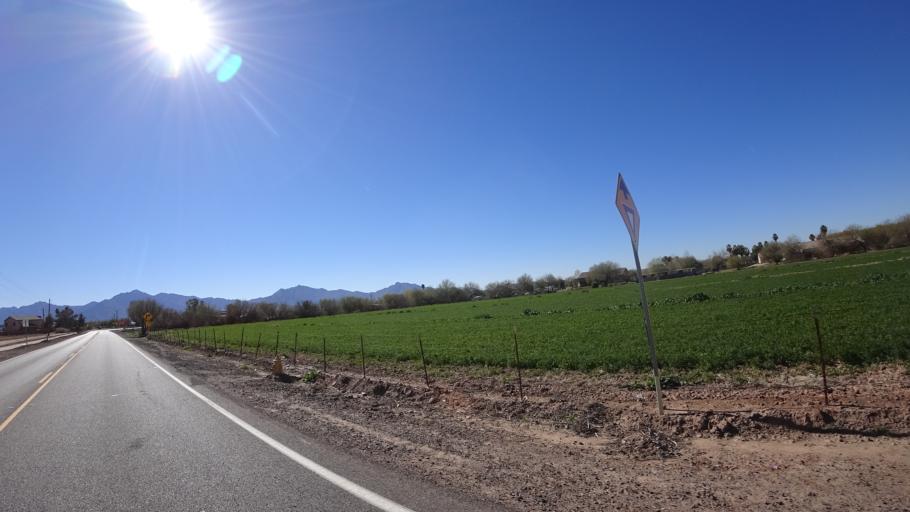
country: US
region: Arizona
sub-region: Maricopa County
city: Tolleson
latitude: 33.3944
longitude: -112.2722
